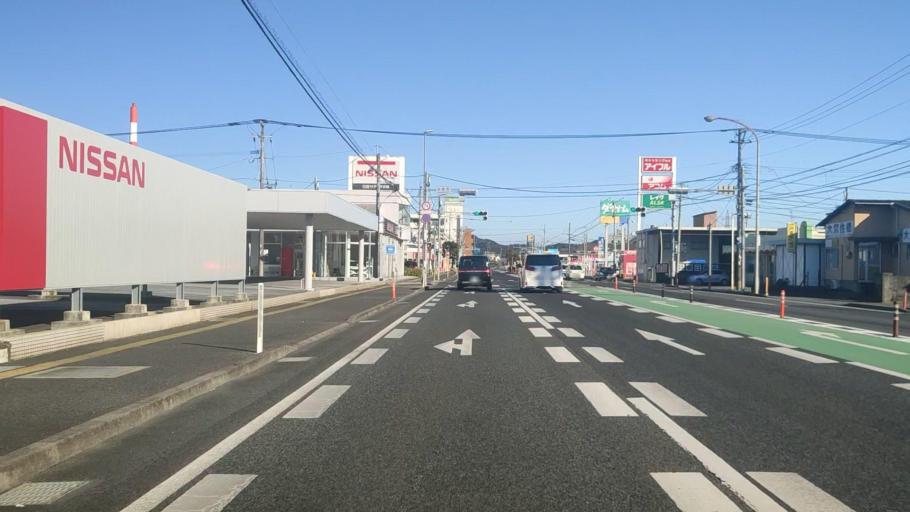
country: JP
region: Miyazaki
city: Nobeoka
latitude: 32.5929
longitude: 131.6764
